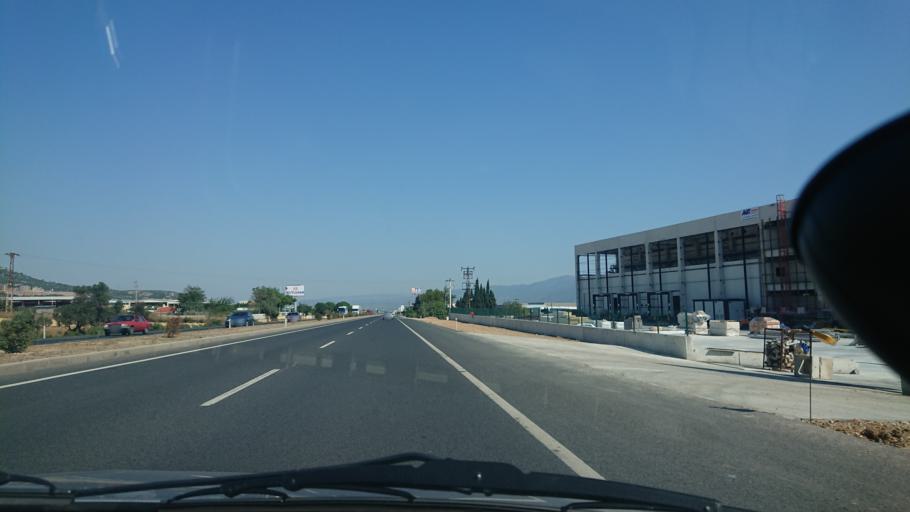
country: TR
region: Izmir
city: Kemalpasa
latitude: 38.4524
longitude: 27.4698
